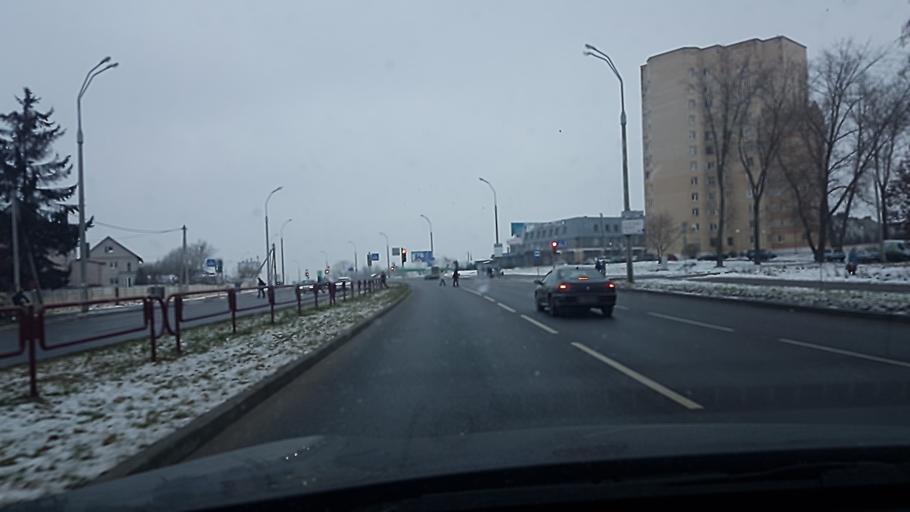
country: BY
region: Minsk
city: Bal'shavik
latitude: 53.9578
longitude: 27.5361
